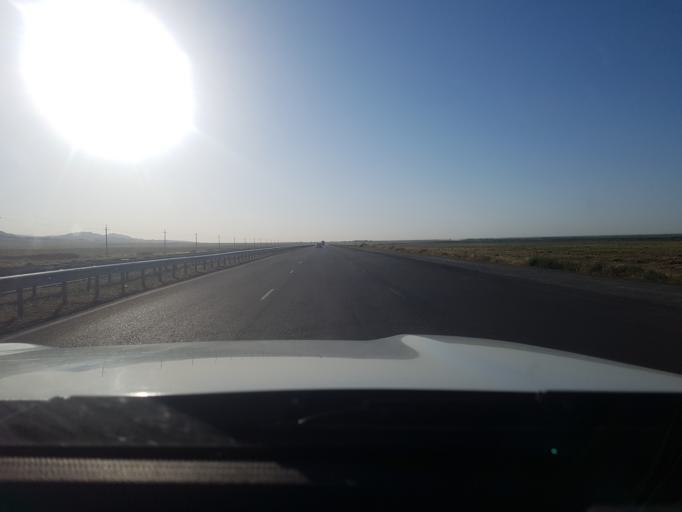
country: IR
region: Razavi Khorasan
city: Dargaz
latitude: 37.7020
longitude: 59.0412
